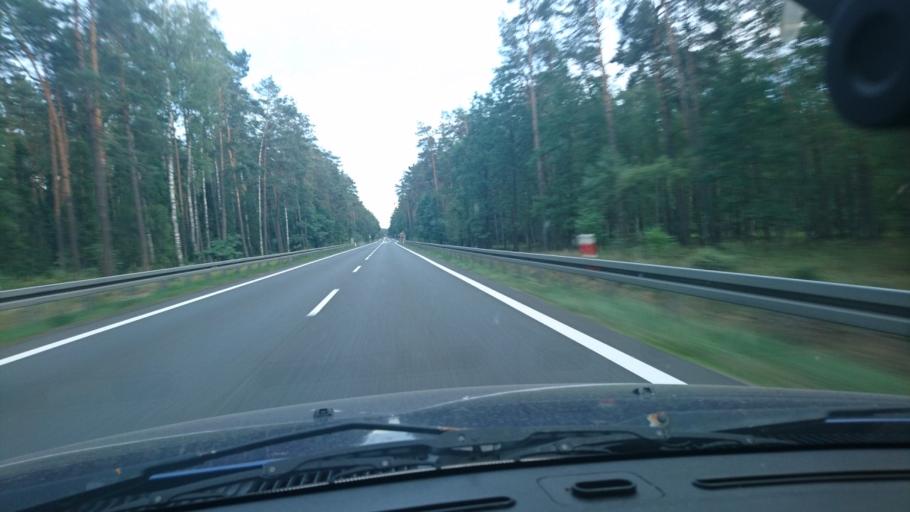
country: PL
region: Silesian Voivodeship
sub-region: Powiat lubliniecki
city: Lubliniec
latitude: 50.6141
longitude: 18.6913
